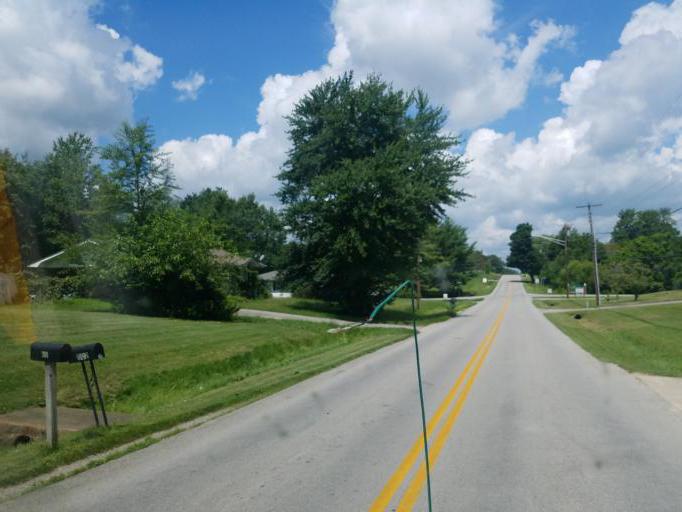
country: US
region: Kentucky
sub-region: Grayson County
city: Leitchfield
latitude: 37.4917
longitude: -86.2965
